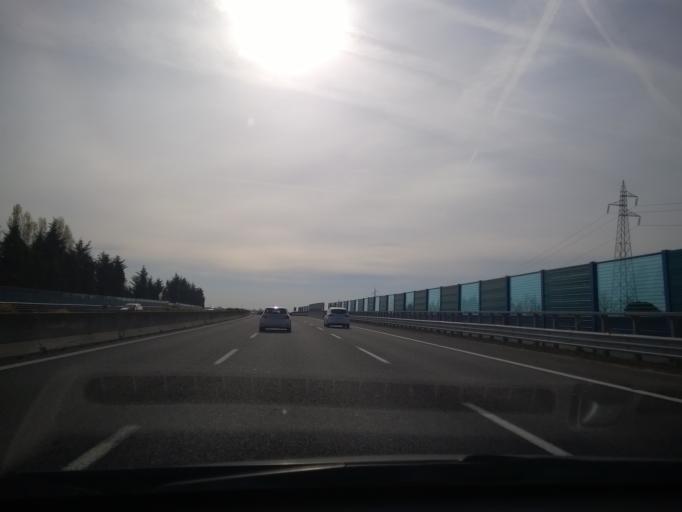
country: IT
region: Emilia-Romagna
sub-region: Forli-Cesena
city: Forli
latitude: 44.2835
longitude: 12.0063
